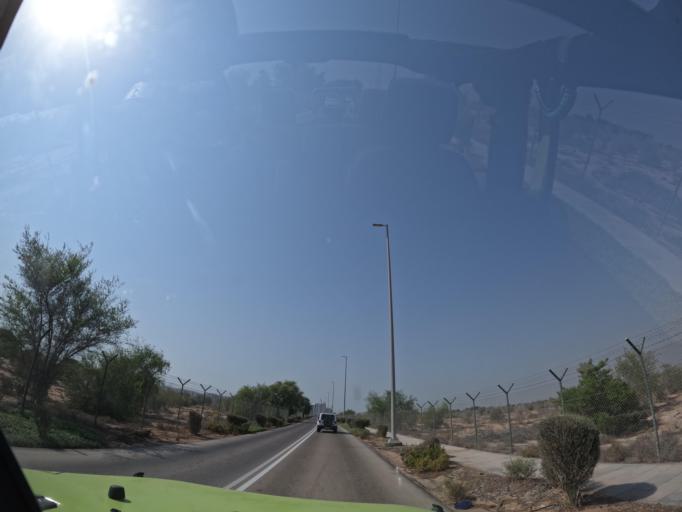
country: AE
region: Abu Dhabi
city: Abu Dhabi
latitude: 24.4758
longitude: 54.6278
